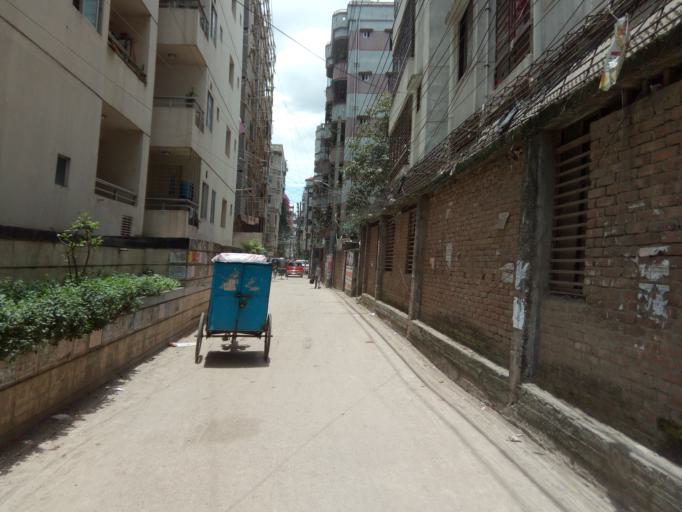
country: BD
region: Dhaka
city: Azimpur
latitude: 23.7417
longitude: 90.3895
